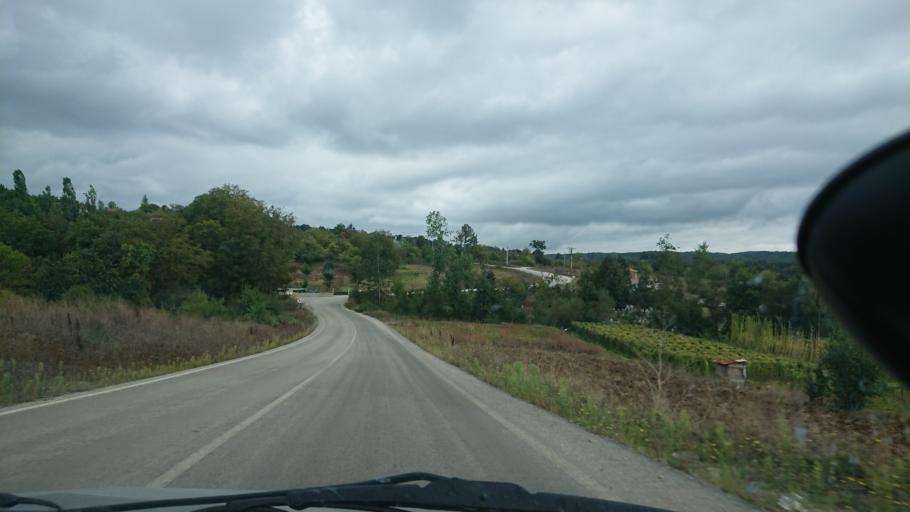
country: TR
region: Bilecik
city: Pazaryeri
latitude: 40.0103
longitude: 29.8038
